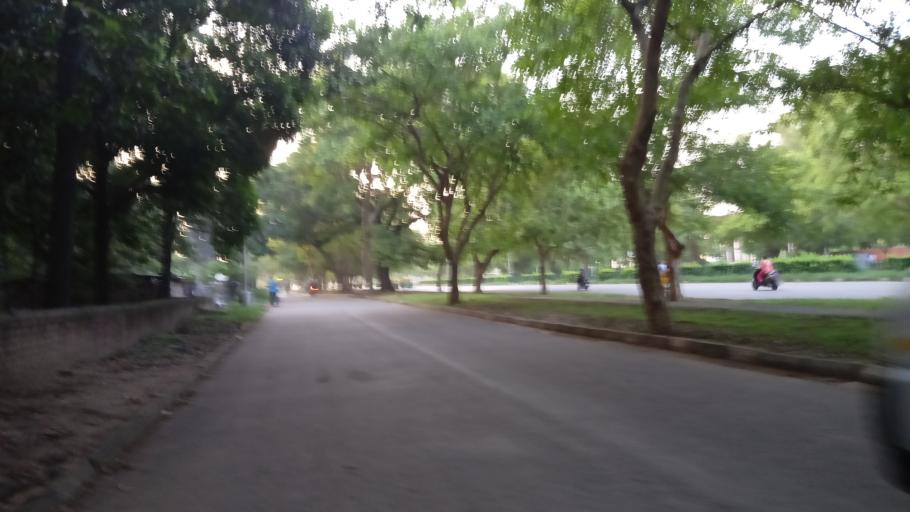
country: IN
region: Chandigarh
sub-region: Chandigarh
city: Chandigarh
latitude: 30.7467
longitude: 76.7521
